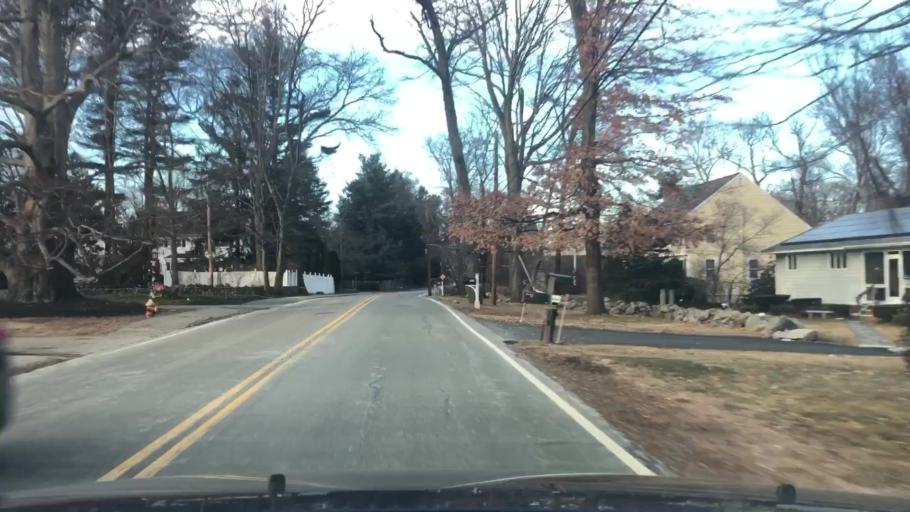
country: US
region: Massachusetts
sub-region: Essex County
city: Andover
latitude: 42.6736
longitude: -71.1139
